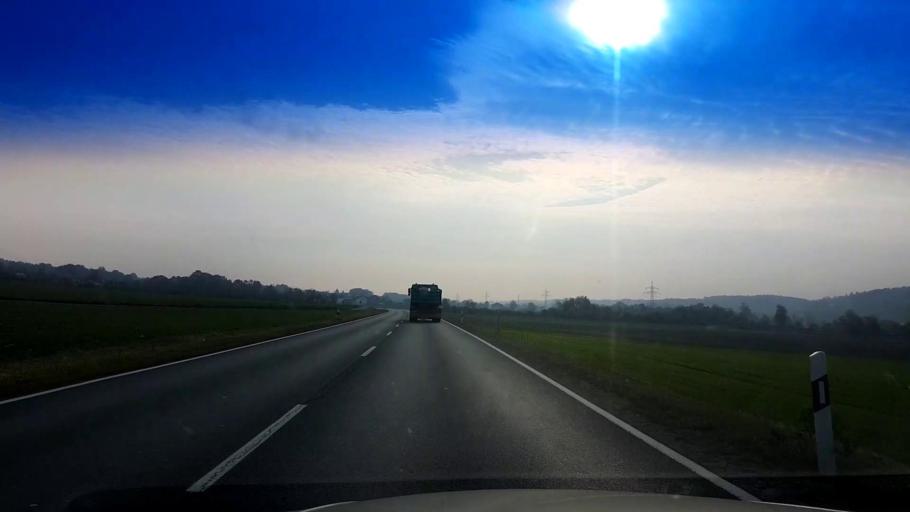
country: DE
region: Bavaria
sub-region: Upper Franconia
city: Mainleus
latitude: 50.1201
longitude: 11.3286
